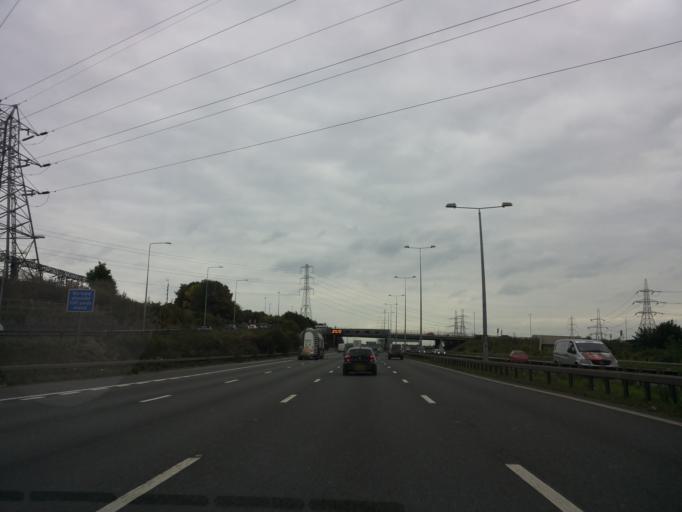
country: GB
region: England
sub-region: Kent
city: Swanscombe
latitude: 51.4279
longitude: 0.3277
